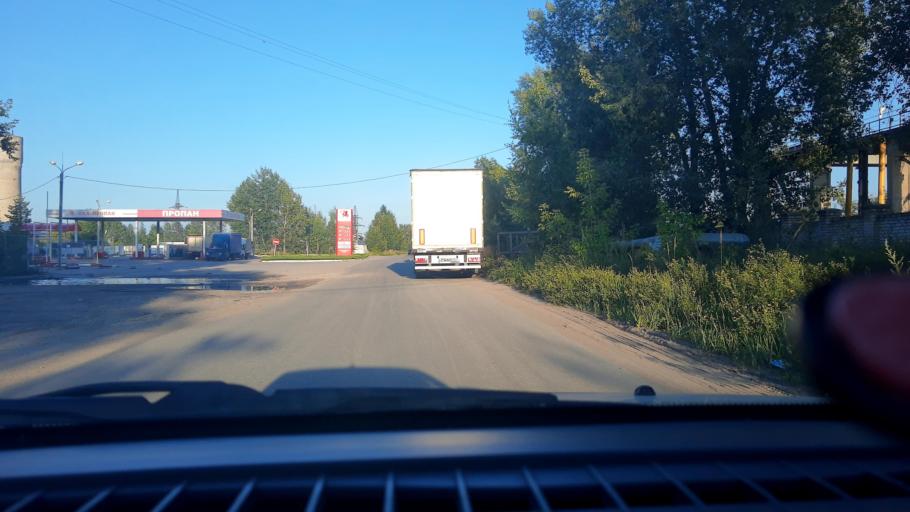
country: RU
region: Nizjnij Novgorod
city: Gorbatovka
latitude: 56.3742
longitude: 43.7912
